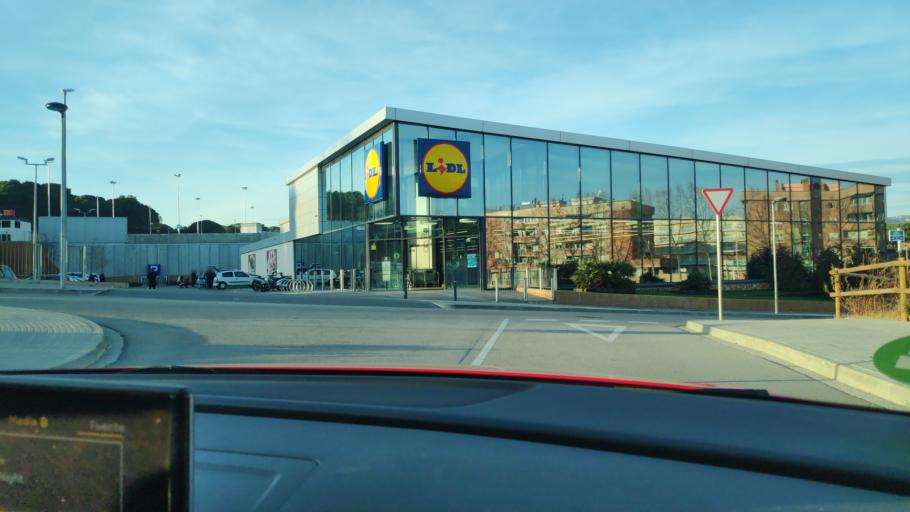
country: ES
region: Catalonia
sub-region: Provincia de Girona
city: Lloret de Mar
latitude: 41.7033
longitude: 2.8354
